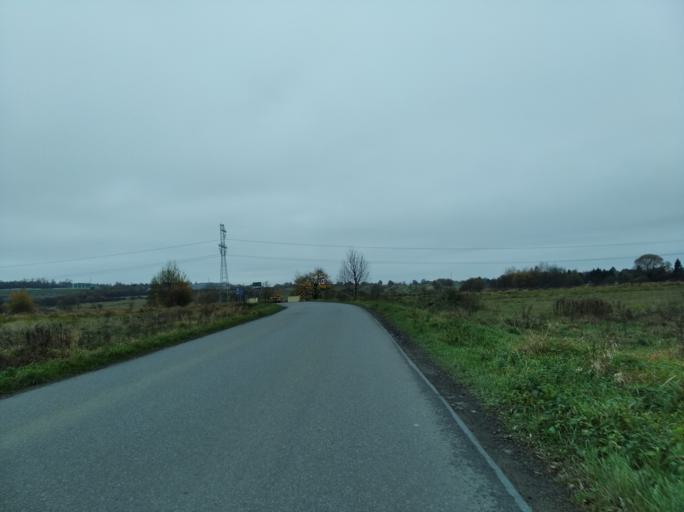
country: PL
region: Subcarpathian Voivodeship
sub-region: Powiat krosnienski
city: Odrzykon
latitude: 49.7217
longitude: 21.7622
